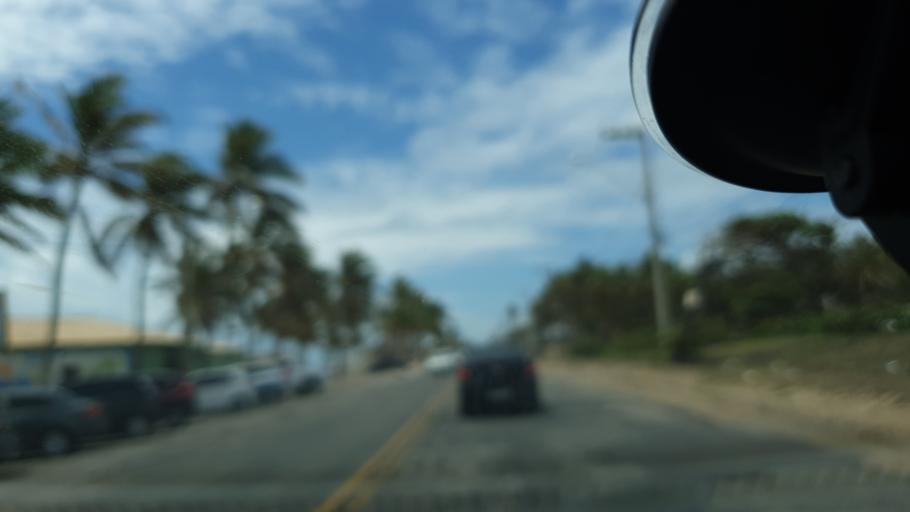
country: BR
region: Sergipe
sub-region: Sao Cristovao
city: Sao Cristovao
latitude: -11.0456
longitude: -37.0887
